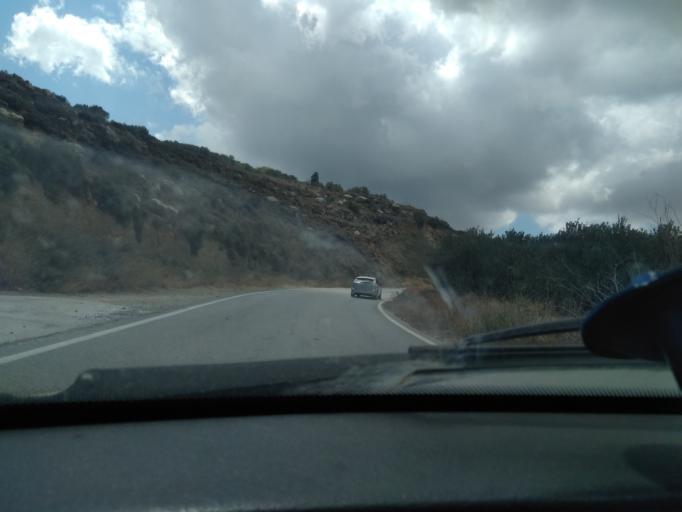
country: GR
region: Crete
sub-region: Nomos Lasithiou
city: Siteia
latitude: 35.0967
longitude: 26.0714
